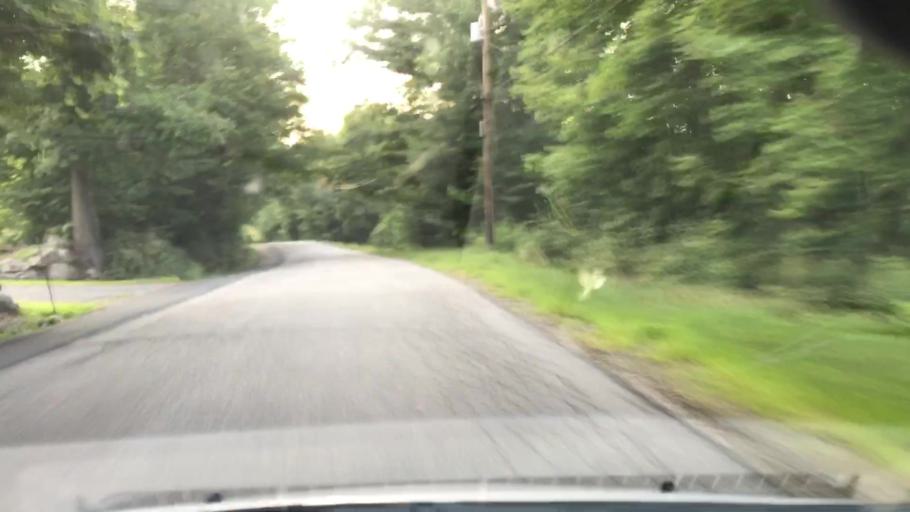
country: US
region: New Hampshire
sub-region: Grafton County
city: North Haverhill
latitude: 44.0714
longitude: -72.0130
